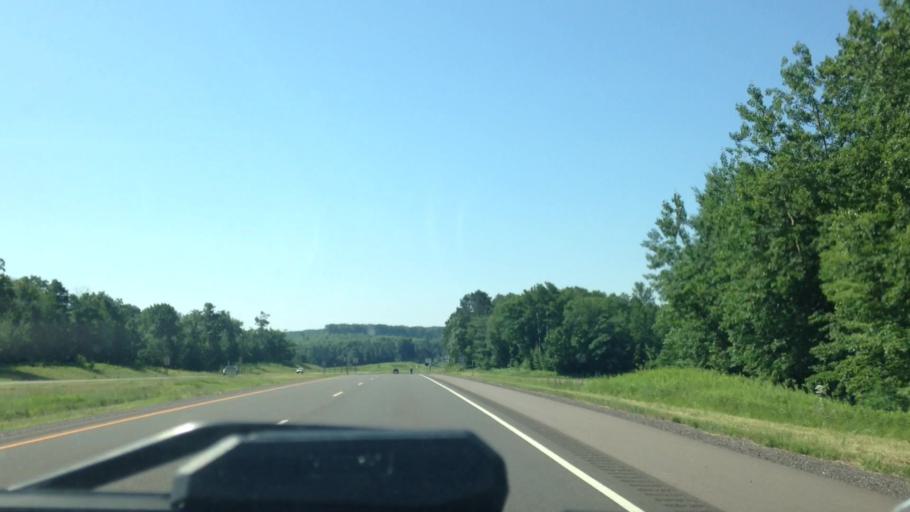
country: US
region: Wisconsin
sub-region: Washburn County
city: Spooner
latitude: 45.9856
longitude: -91.8287
